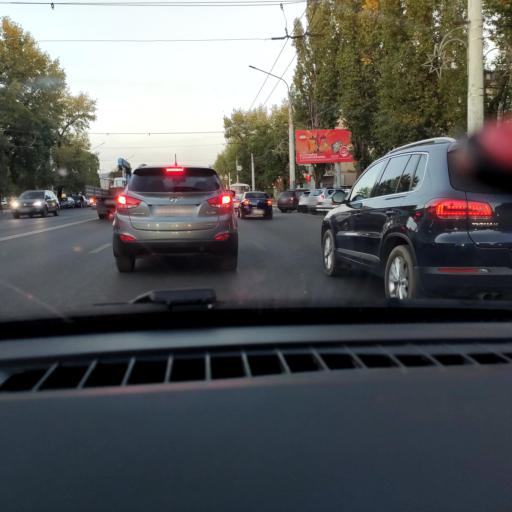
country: RU
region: Voronezj
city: Voronezh
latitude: 51.6544
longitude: 39.2434
